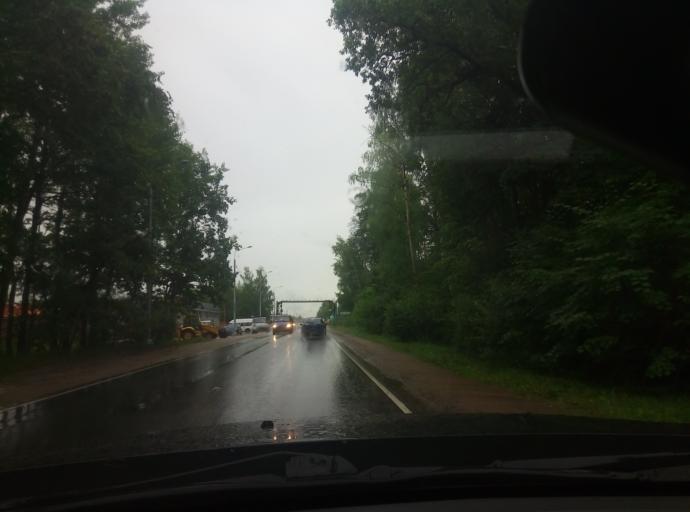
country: RU
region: Moskovskaya
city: Protvino
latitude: 54.8852
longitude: 37.1933
